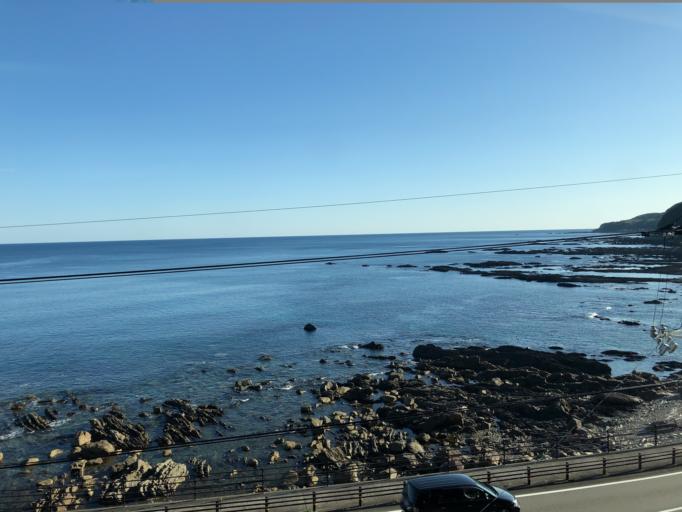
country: JP
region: Kochi
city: Nakamura
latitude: 33.0506
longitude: 133.0969
